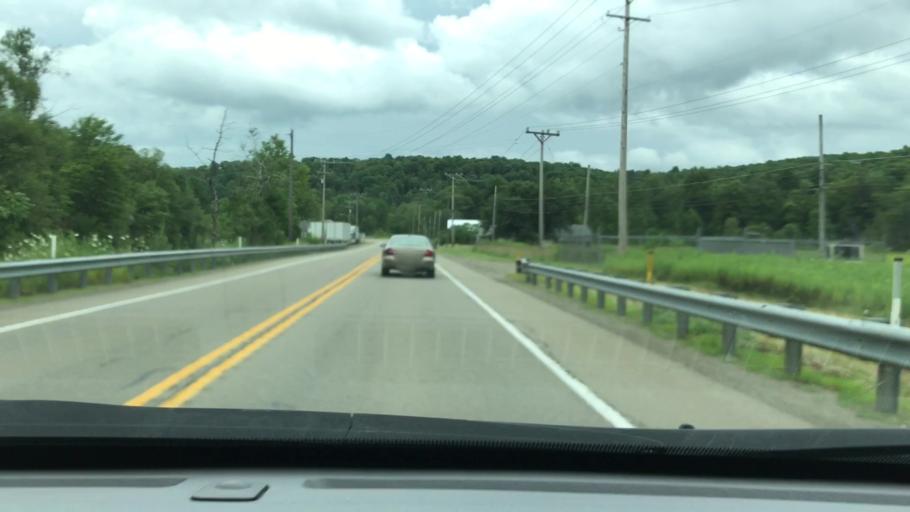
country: US
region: Pennsylvania
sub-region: Elk County
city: Johnsonburg
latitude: 41.5209
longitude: -78.6779
